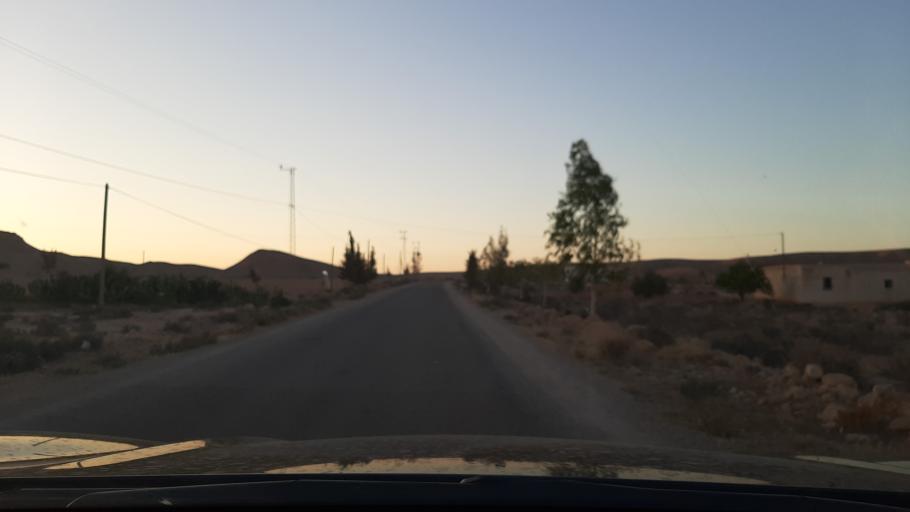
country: TN
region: Qabis
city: Matmata
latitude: 33.5677
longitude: 10.1777
